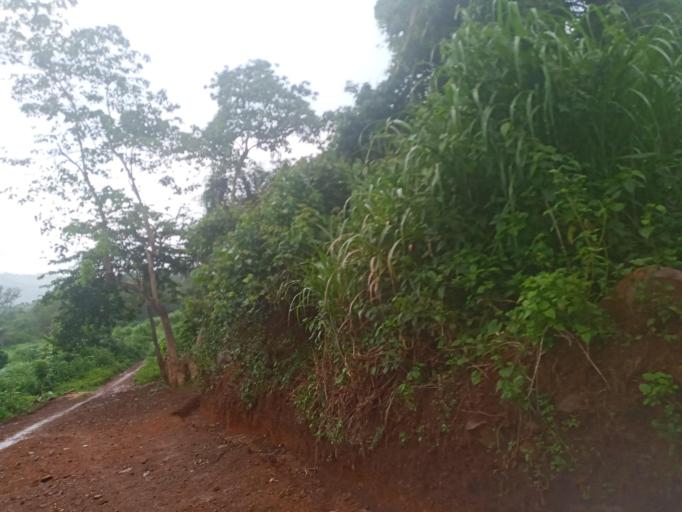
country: SL
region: Northern Province
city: Bumbuna
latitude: 8.9203
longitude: -11.7418
